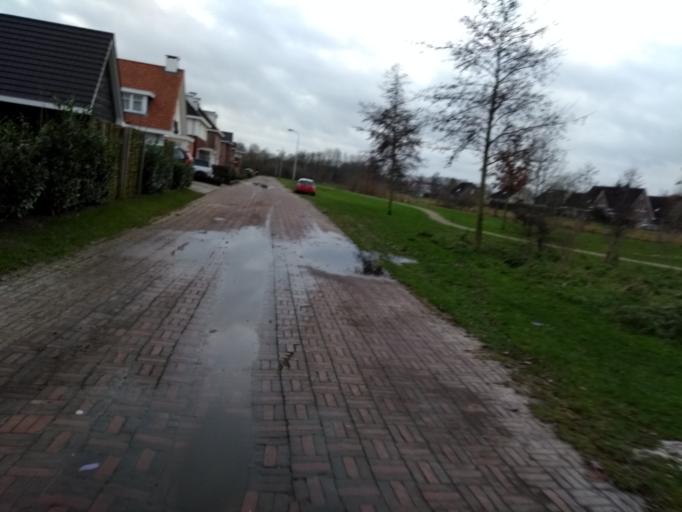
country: NL
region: Overijssel
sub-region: Gemeente Almelo
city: Almelo
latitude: 52.3729
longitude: 6.6987
